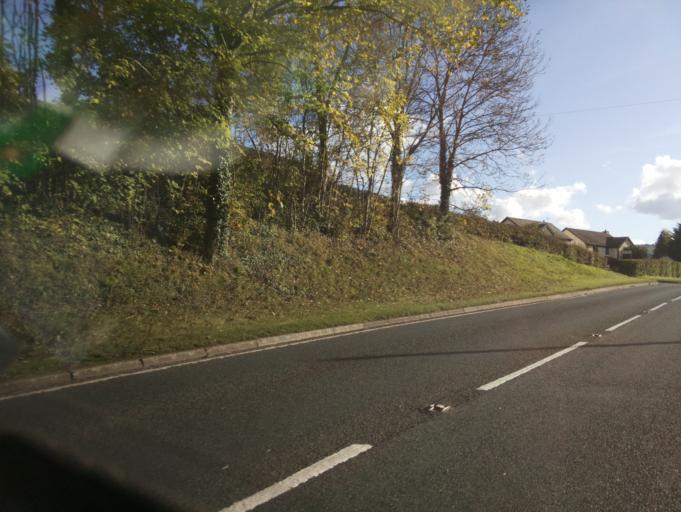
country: GB
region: Wales
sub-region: Sir Powys
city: Hay
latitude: 52.0373
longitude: -3.2024
